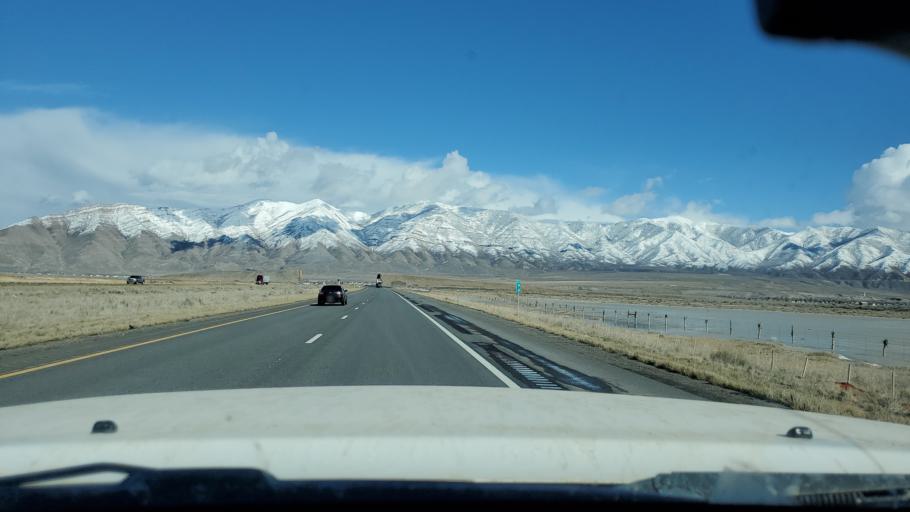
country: US
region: Utah
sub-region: Tooele County
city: Stansbury park
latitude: 40.6616
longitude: -112.3392
